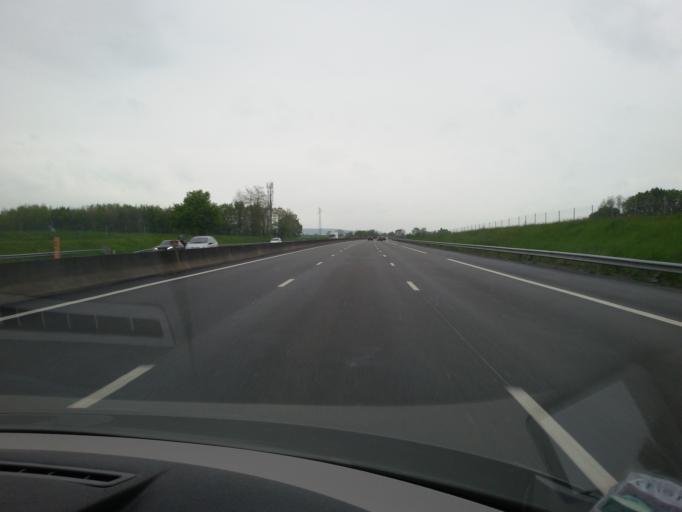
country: FR
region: Rhone-Alpes
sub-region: Departement de l'Ain
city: Pont-de-Vaux
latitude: 46.4564
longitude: 4.8747
